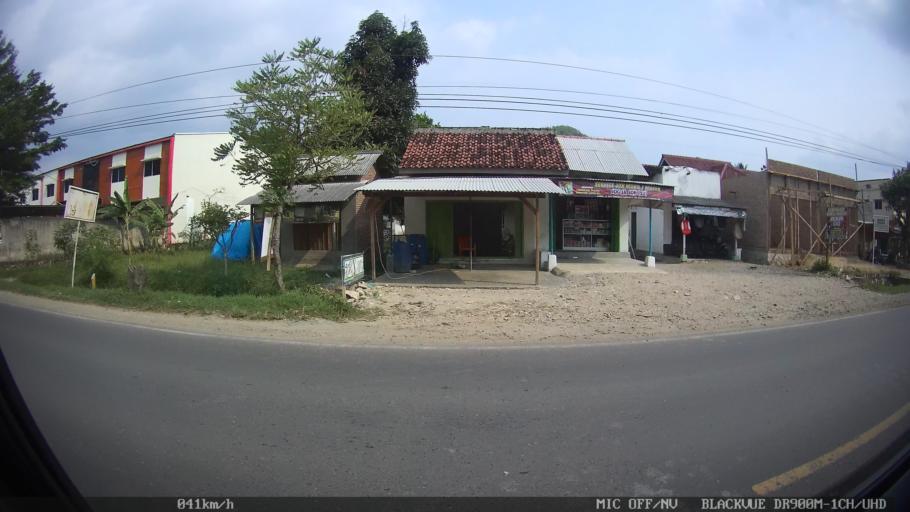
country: ID
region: Lampung
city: Gadingrejo
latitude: -5.3820
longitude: 105.0218
